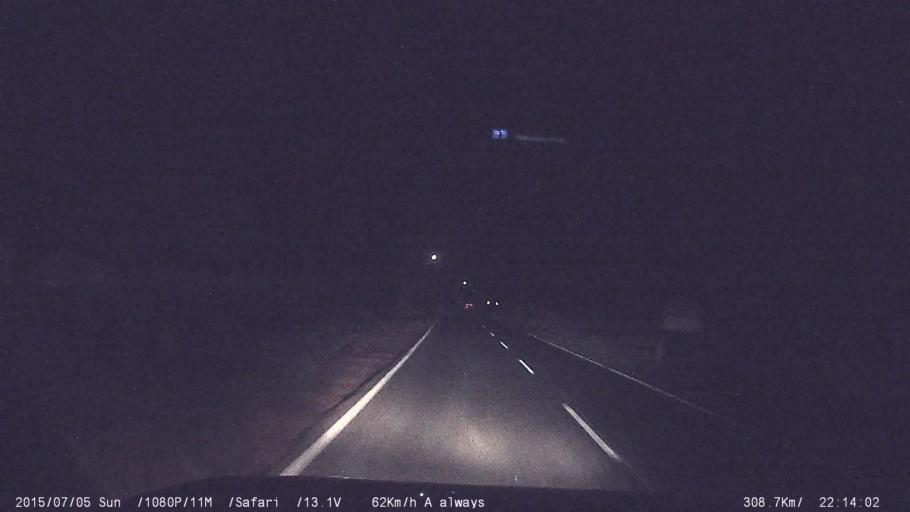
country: IN
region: Kerala
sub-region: Palakkad district
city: Palakkad
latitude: 10.8690
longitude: 76.5547
